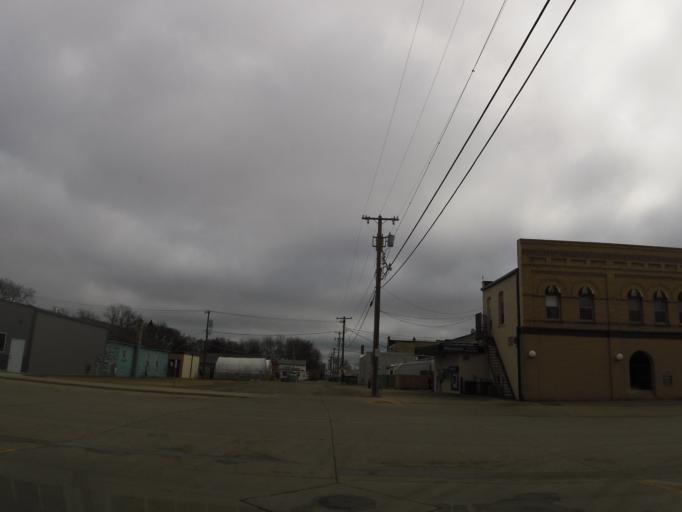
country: US
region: North Dakota
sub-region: Cass County
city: Casselton
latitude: 46.9011
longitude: -97.2116
